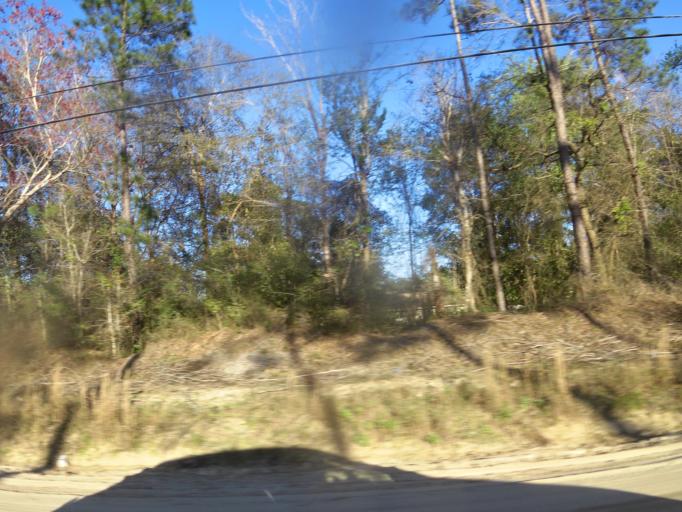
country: US
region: Florida
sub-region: Clay County
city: Middleburg
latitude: 30.1239
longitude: -81.8818
